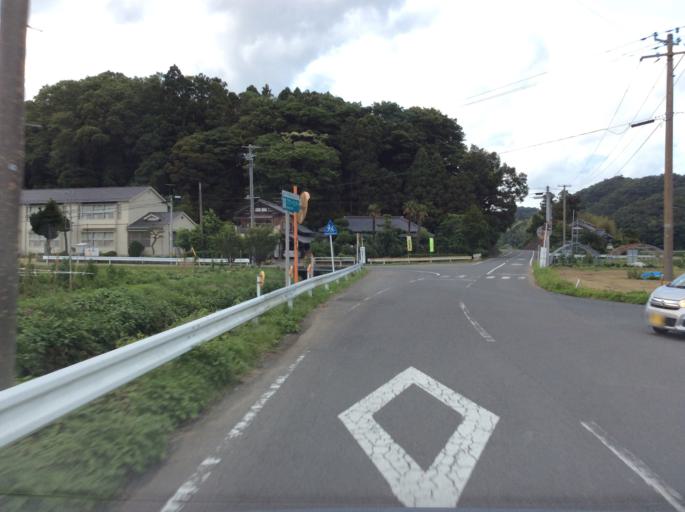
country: JP
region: Fukushima
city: Iwaki
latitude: 37.0907
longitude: 140.9407
